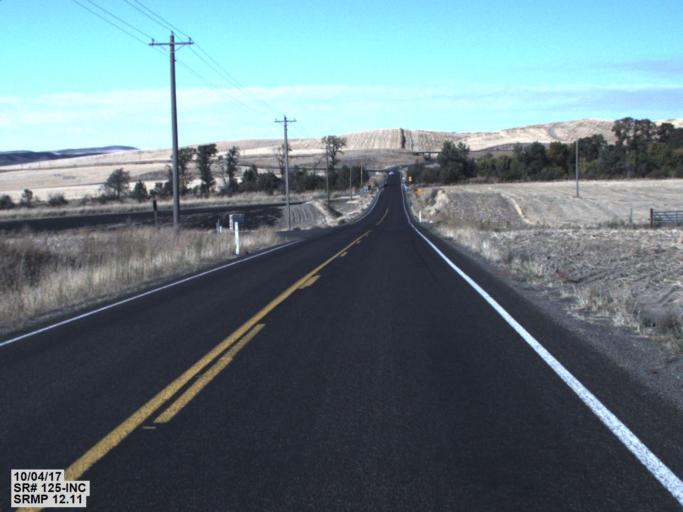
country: US
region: Washington
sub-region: Walla Walla County
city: Walla Walla
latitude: 46.1470
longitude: -118.3726
